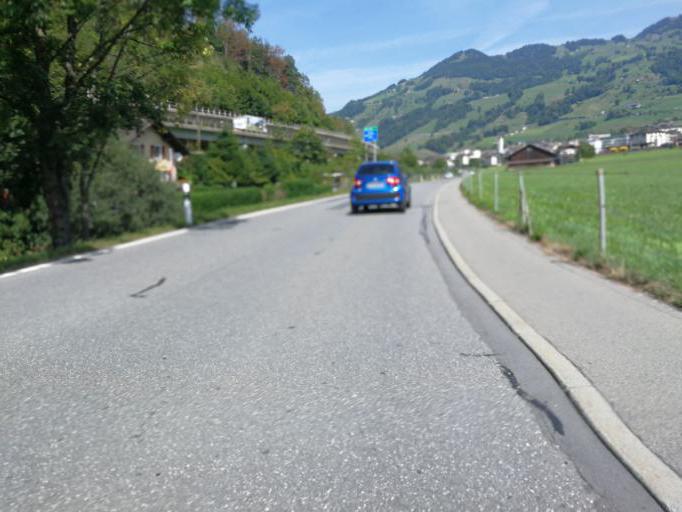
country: CH
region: Schwyz
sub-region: Bezirk Schwyz
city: Ibach
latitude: 47.0219
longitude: 8.6290
